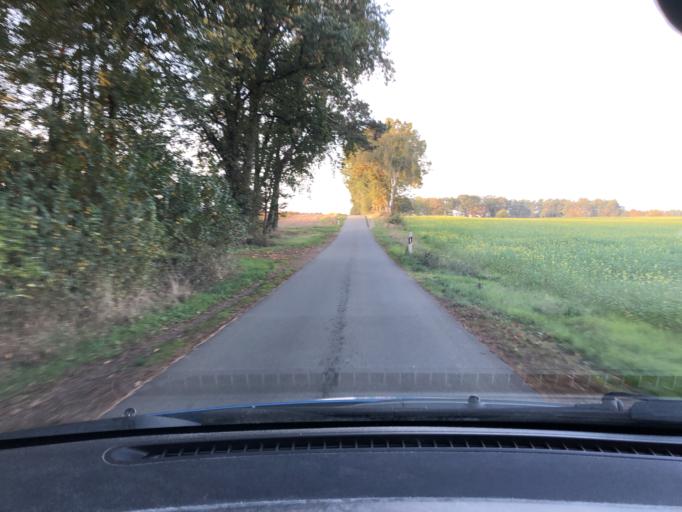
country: DE
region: Lower Saxony
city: Hitzacker
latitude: 53.1340
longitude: 11.0087
